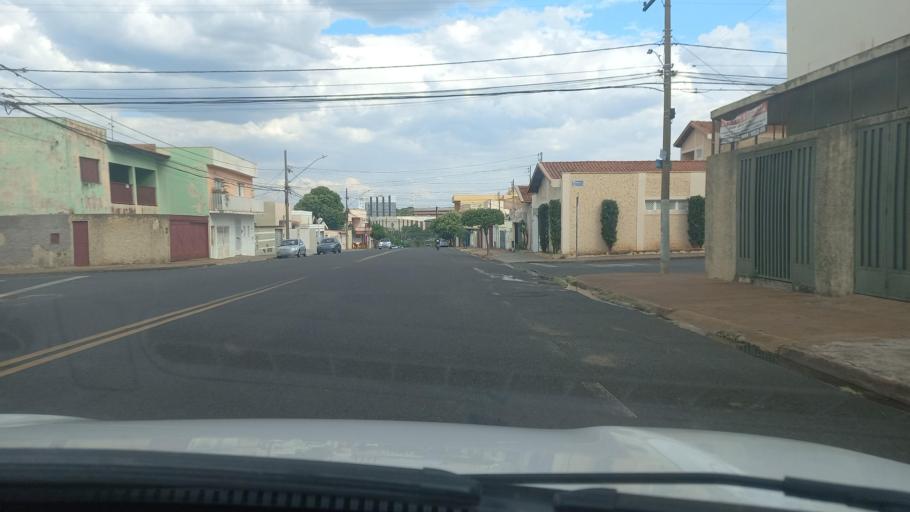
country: BR
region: Minas Gerais
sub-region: Uberaba
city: Uberaba
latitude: -19.7626
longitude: -47.9537
